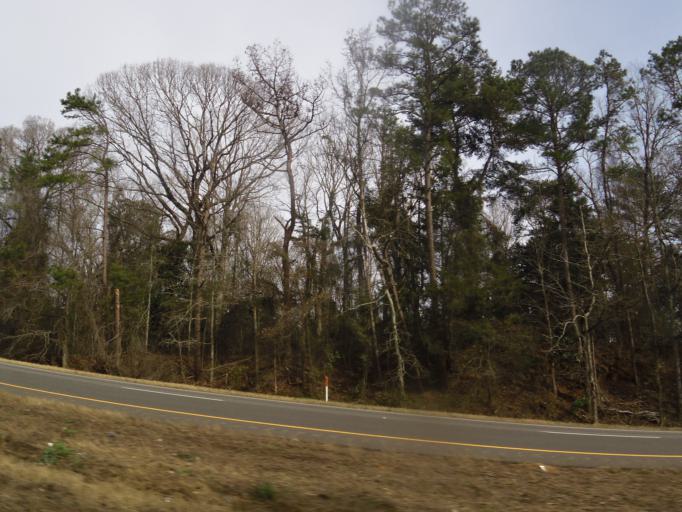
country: US
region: Alabama
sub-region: Dale County
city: Ozark
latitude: 31.5253
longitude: -85.7178
